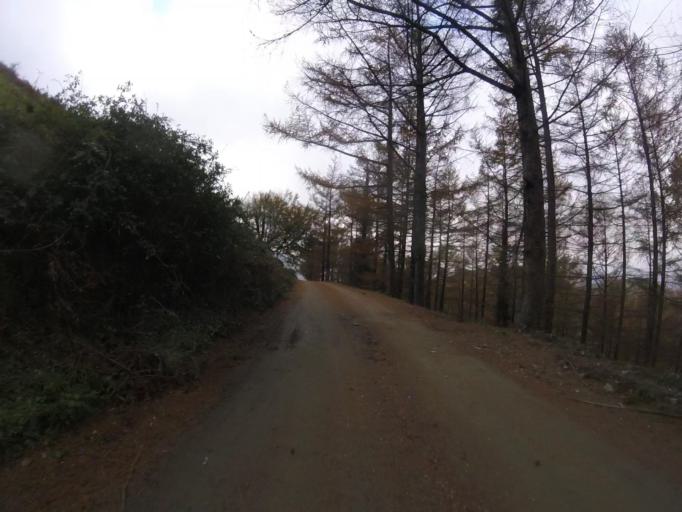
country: ES
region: Navarre
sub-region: Provincia de Navarra
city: Goizueta
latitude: 43.2023
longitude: -1.8293
